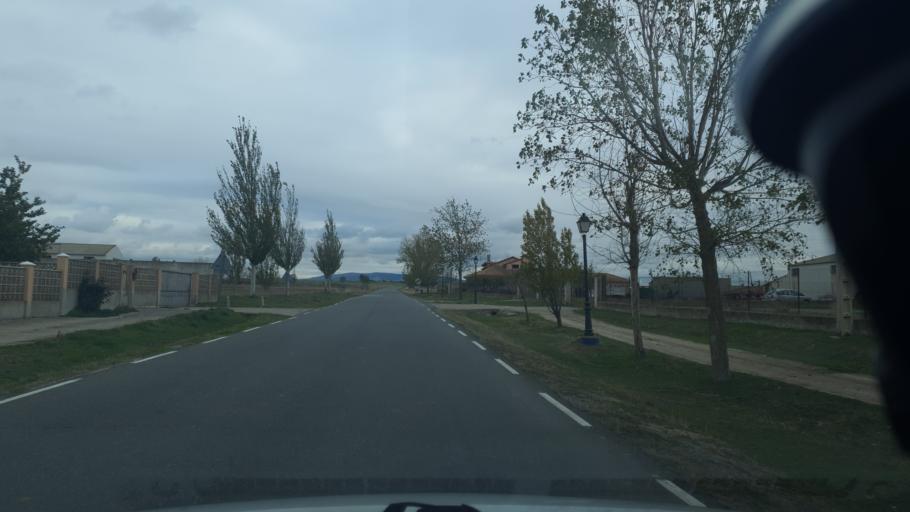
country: ES
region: Castille and Leon
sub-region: Provincia de Avila
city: Velayos
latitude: 40.8394
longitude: -4.6211
